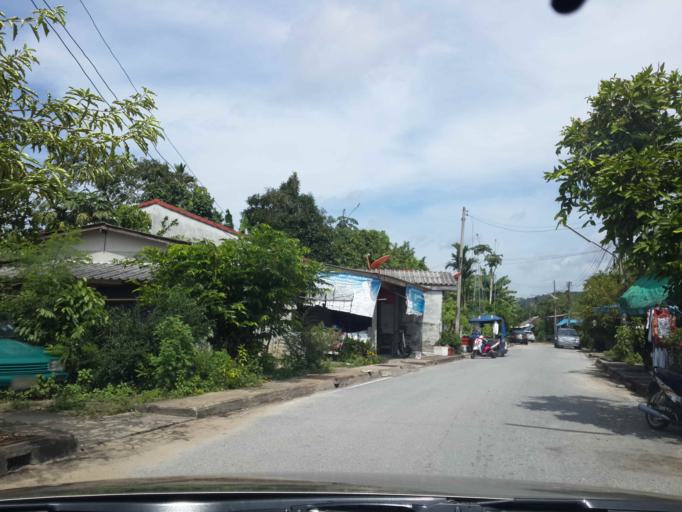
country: TH
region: Narathiwat
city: Rueso
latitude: 6.3968
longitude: 101.5163
